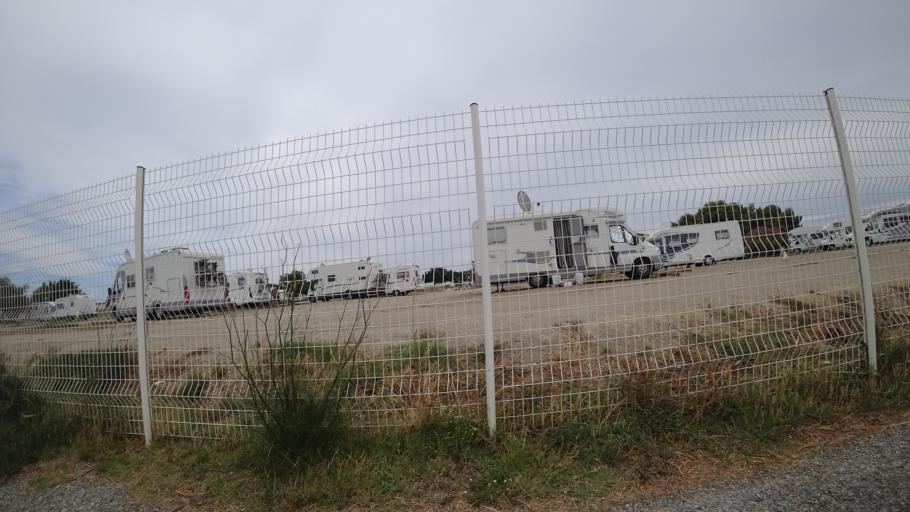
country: FR
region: Languedoc-Roussillon
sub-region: Departement des Pyrenees-Orientales
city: Le Barcares
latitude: 42.8017
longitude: 3.0322
